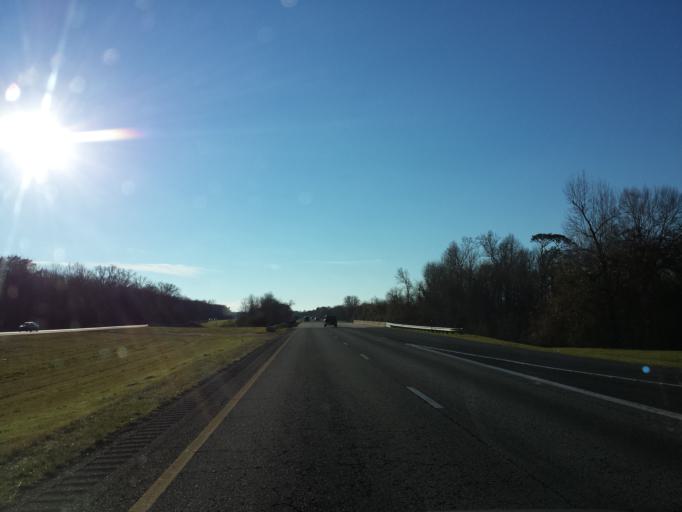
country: US
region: Alabama
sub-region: Tuscaloosa County
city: Tuscaloosa
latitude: 33.1522
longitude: -87.6011
